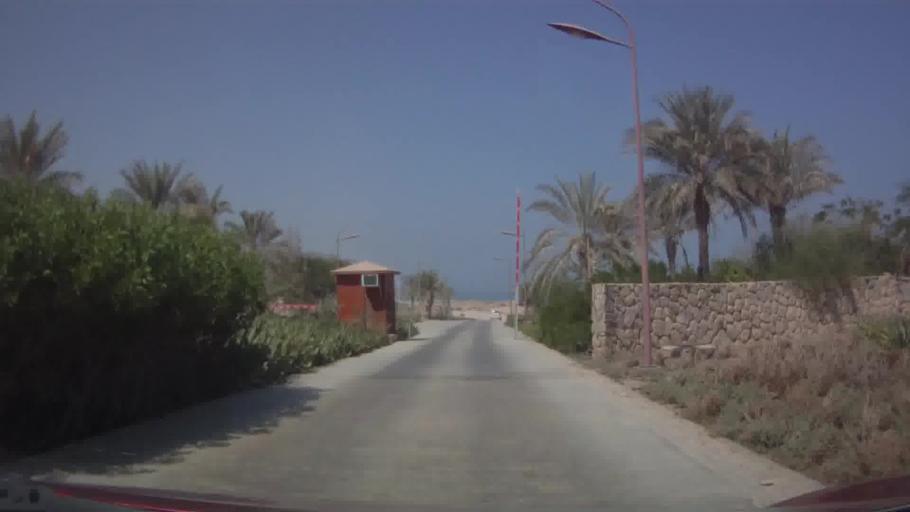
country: OM
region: Muhafazat Masqat
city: Muscat
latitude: 23.4144
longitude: 58.7851
